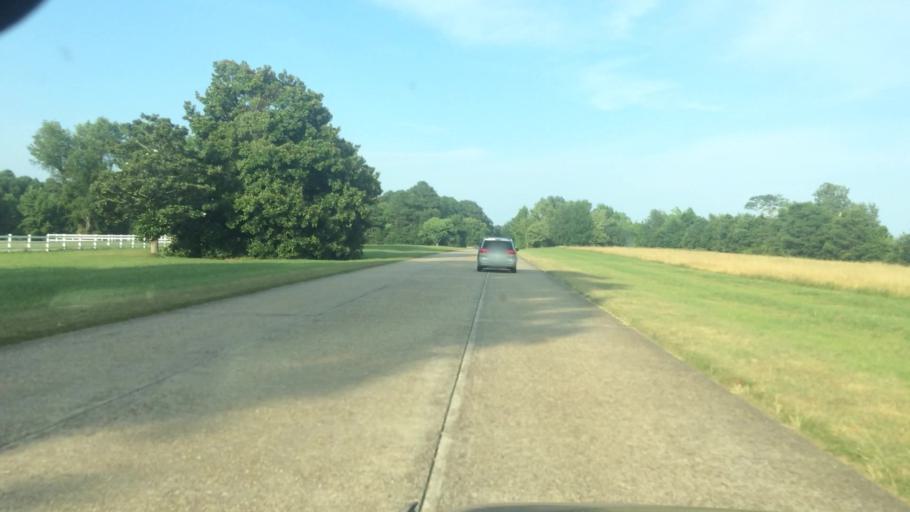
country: US
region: Virginia
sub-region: City of Williamsburg
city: Williamsburg
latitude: 37.2144
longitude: -76.7234
